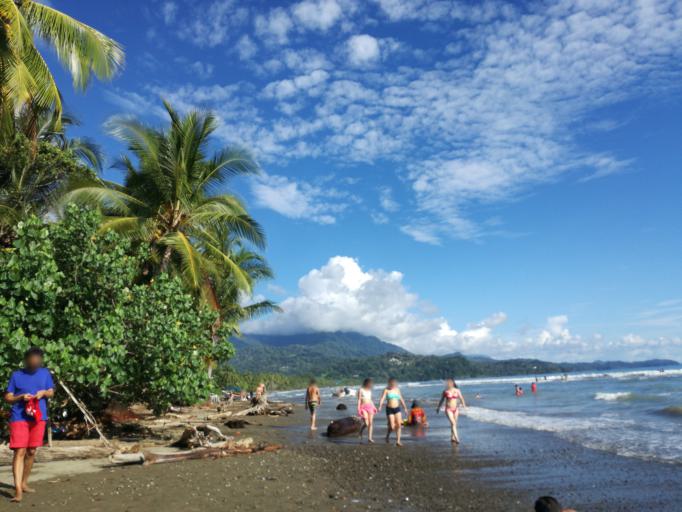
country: CR
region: San Jose
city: Daniel Flores
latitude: 9.1539
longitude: -83.7513
